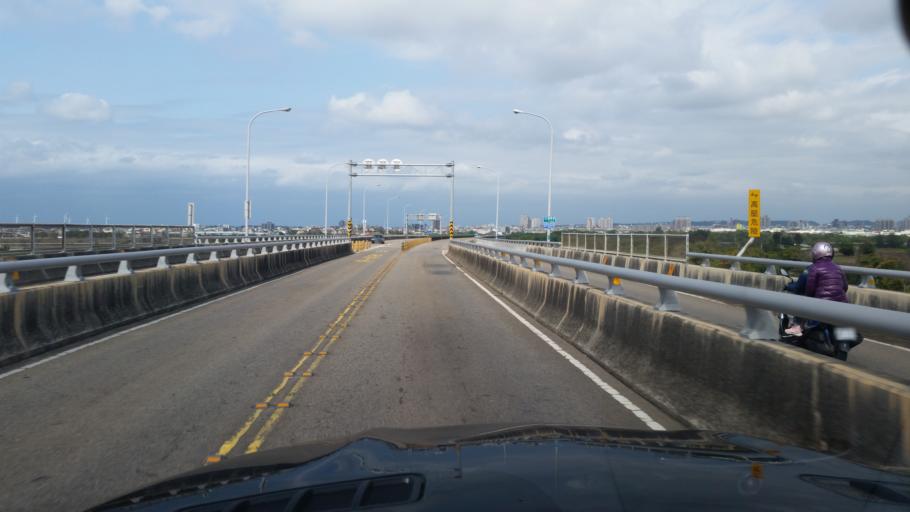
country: TW
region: Taiwan
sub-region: Miaoli
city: Miaoli
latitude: 24.6590
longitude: 120.8667
